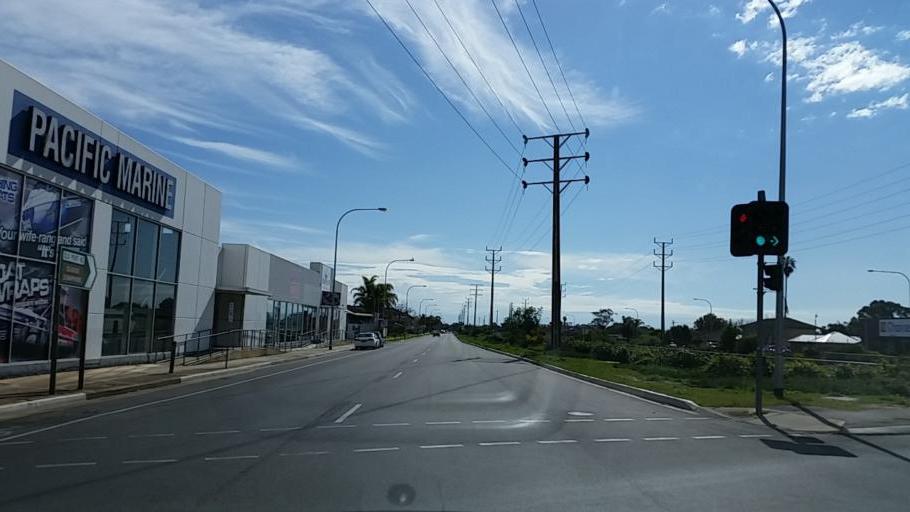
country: AU
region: South Australia
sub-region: Port Adelaide Enfield
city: Cheltenham
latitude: -34.8655
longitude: 138.5119
